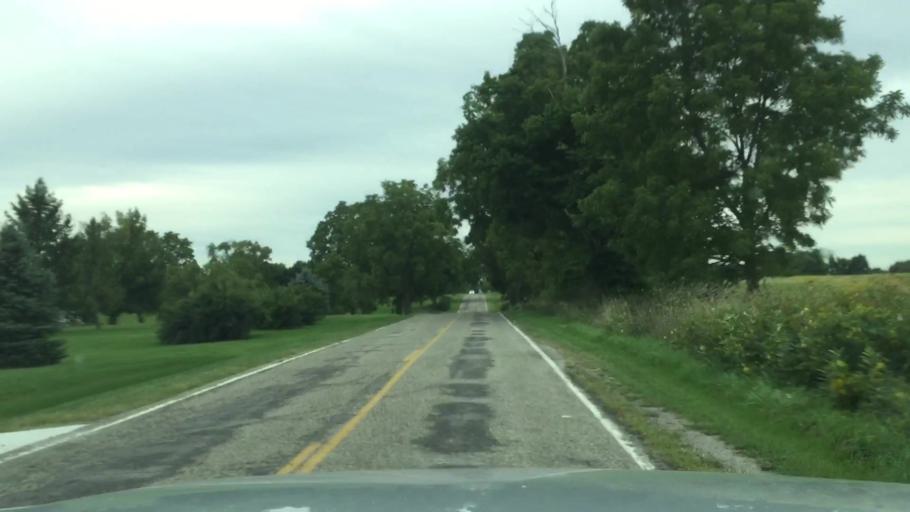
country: US
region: Michigan
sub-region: Shiawassee County
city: Durand
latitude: 42.8966
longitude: -84.0691
